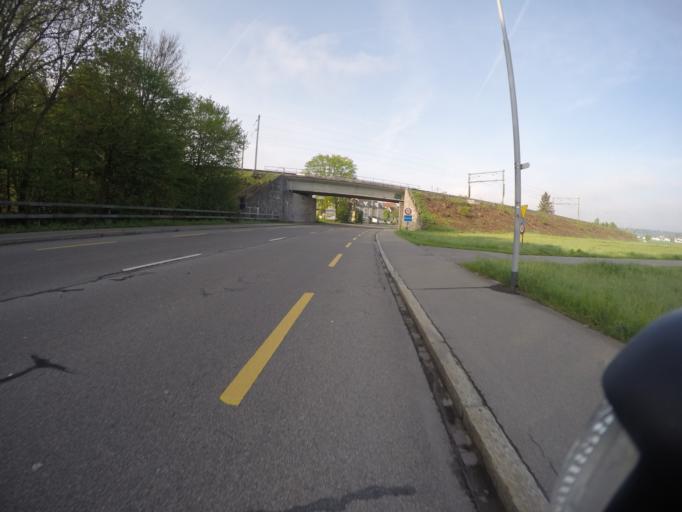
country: CH
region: Zurich
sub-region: Bezirk Uster
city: Bruttisellen
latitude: 47.4267
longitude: 8.6365
